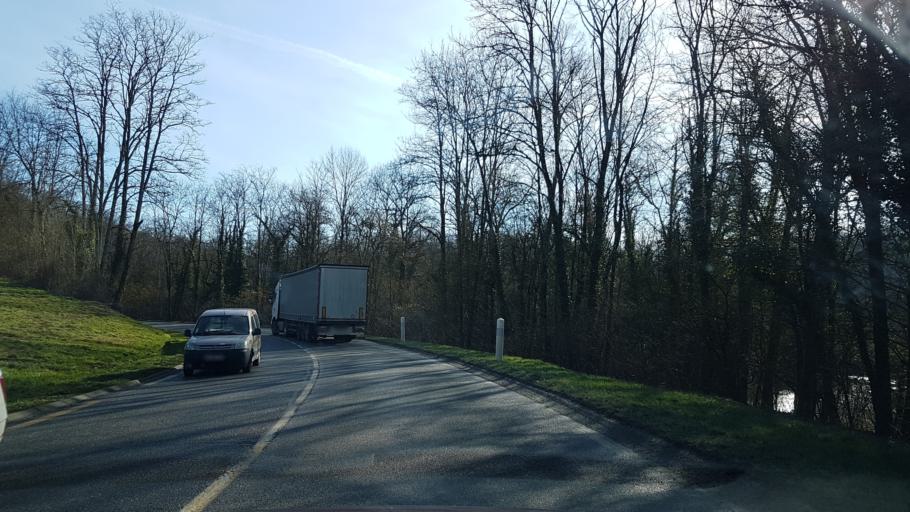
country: FR
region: Rhone-Alpes
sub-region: Departement de la Haute-Savoie
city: Frangy
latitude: 46.0230
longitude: 5.9034
